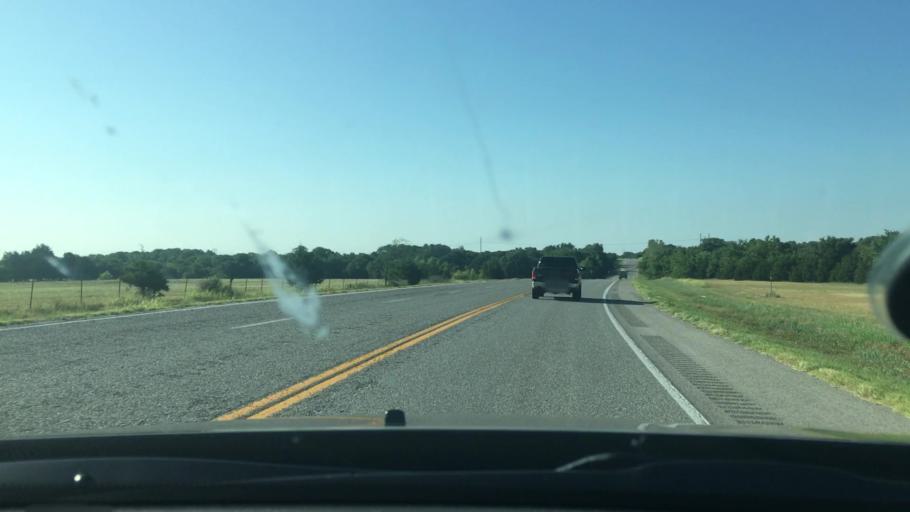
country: US
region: Oklahoma
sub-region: Johnston County
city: Tishomingo
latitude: 34.2730
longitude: -96.7754
